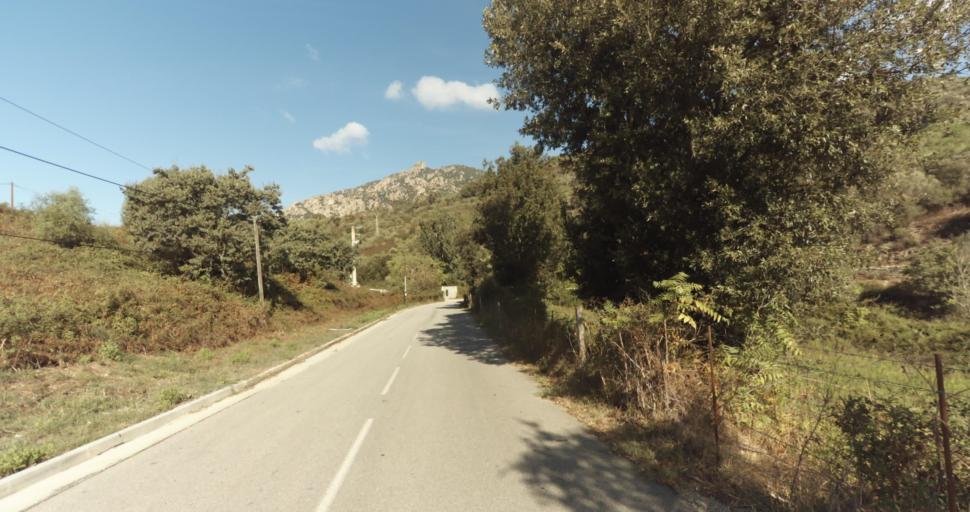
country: FR
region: Corsica
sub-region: Departement de la Corse-du-Sud
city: Ajaccio
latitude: 41.9297
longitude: 8.7018
